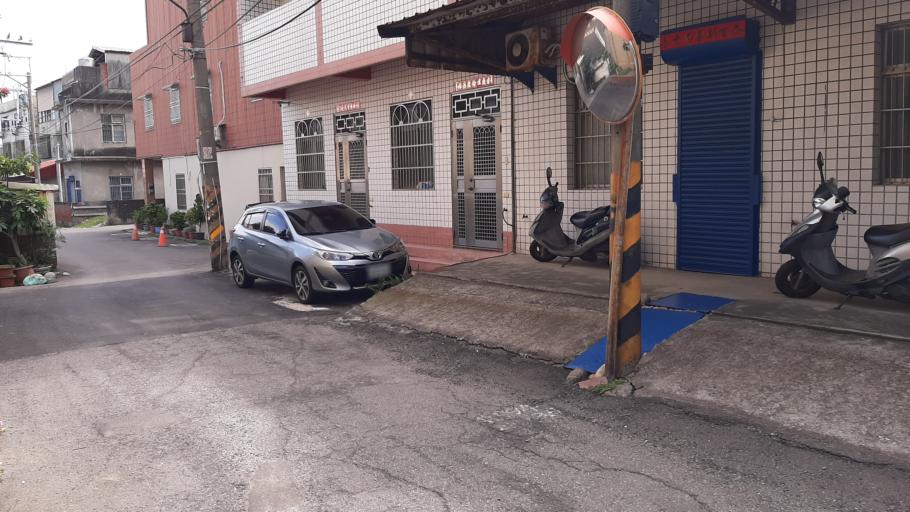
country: TW
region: Taiwan
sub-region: Changhua
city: Chang-hua
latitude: 24.2128
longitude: 120.5484
